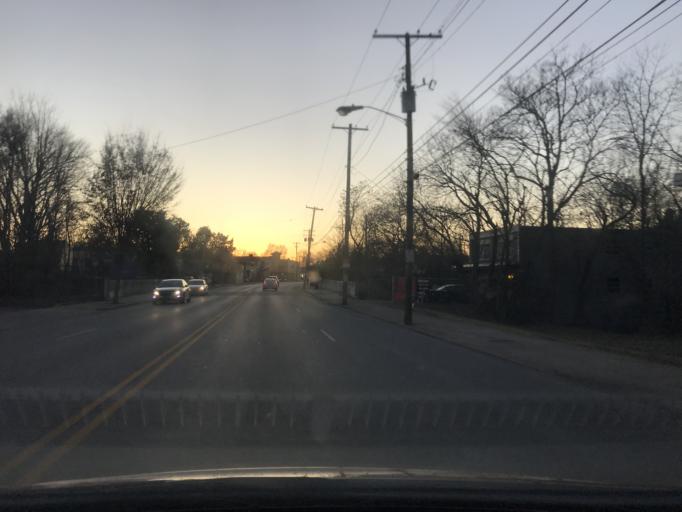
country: US
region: Kentucky
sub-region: Jefferson County
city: Audubon Park
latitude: 38.2348
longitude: -85.7297
